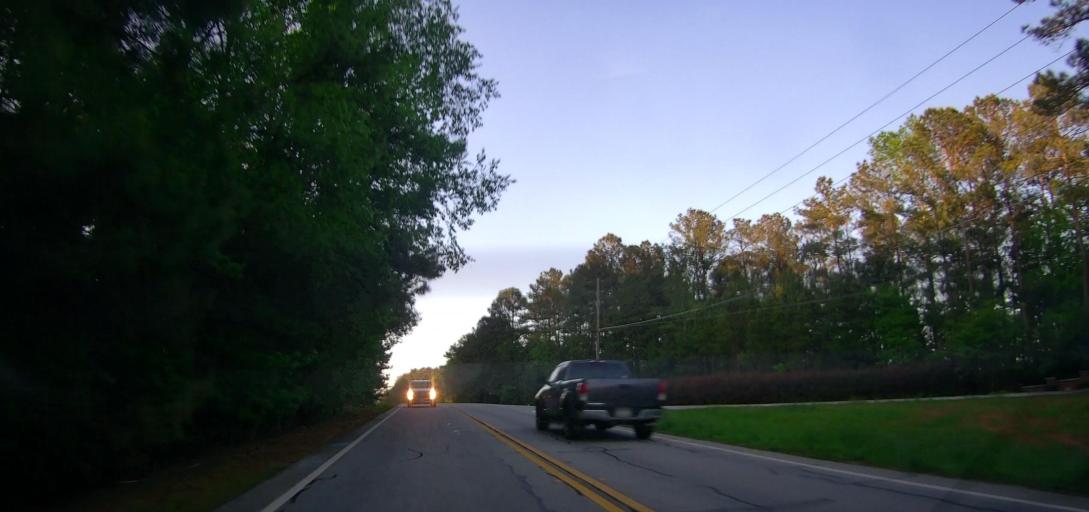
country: US
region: Georgia
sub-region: Newton County
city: Oakwood
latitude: 33.5000
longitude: -83.9499
